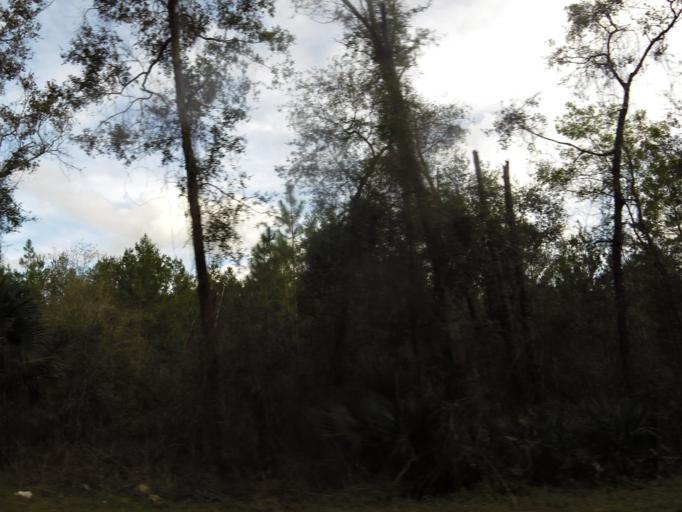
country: US
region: Florida
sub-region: Volusia County
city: Orange City
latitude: 28.9528
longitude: -81.2657
